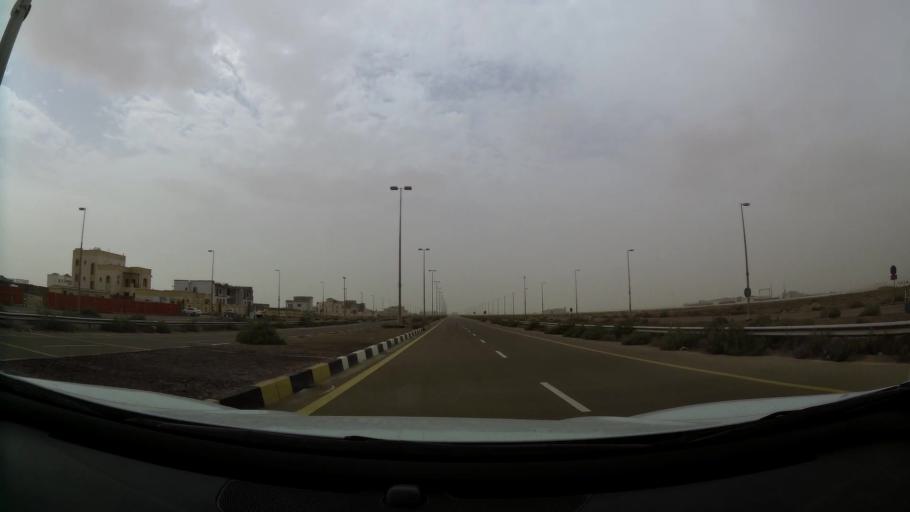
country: AE
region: Abu Dhabi
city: Abu Dhabi
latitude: 24.3746
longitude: 54.6947
